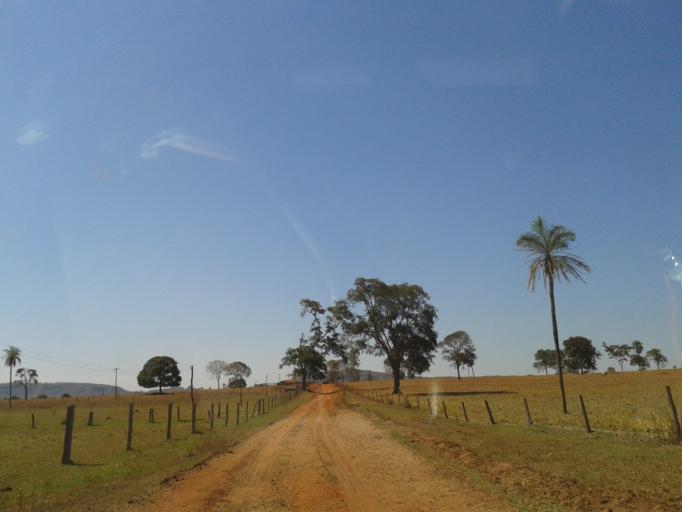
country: BR
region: Minas Gerais
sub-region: Santa Vitoria
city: Santa Vitoria
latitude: -19.0876
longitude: -50.0759
